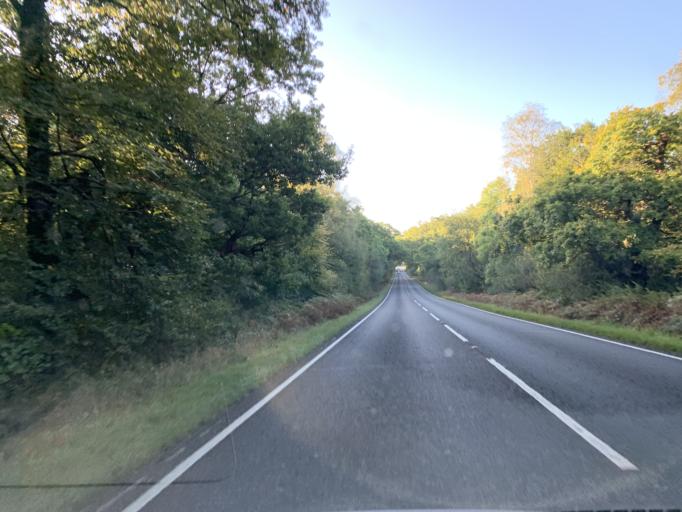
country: GB
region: England
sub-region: Hampshire
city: Lyndhurst
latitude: 50.8477
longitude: -1.5735
